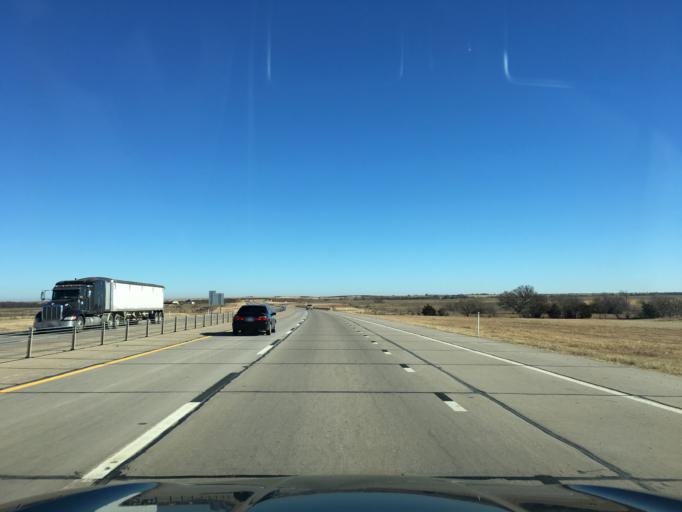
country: US
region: Oklahoma
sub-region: Noble County
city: Perry
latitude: 36.3991
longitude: -97.2772
